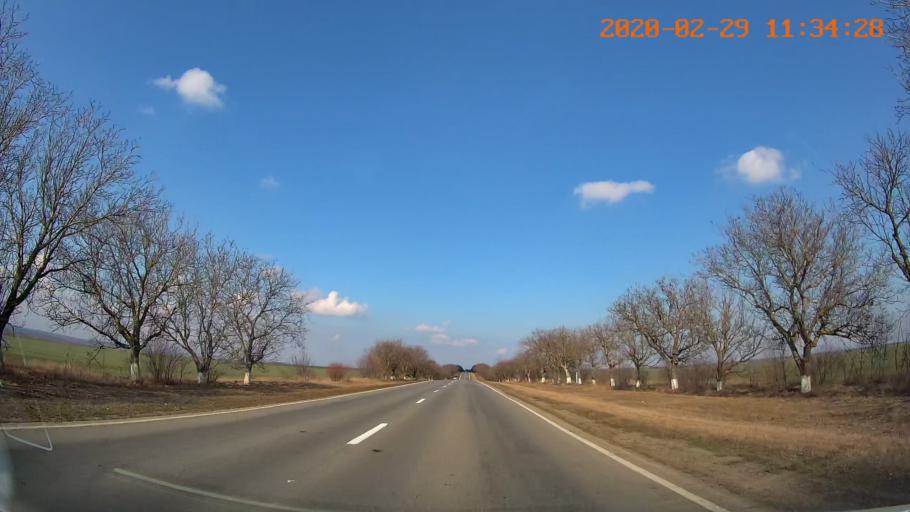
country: MD
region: Rezina
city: Saharna
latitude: 47.5663
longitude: 29.0734
